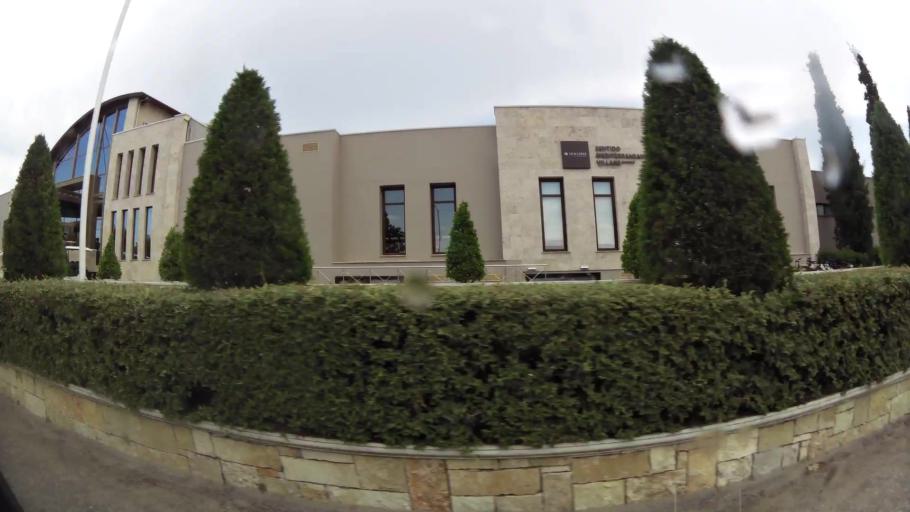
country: GR
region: Central Macedonia
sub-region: Nomos Pierias
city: Paralia
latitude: 40.2861
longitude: 22.6059
